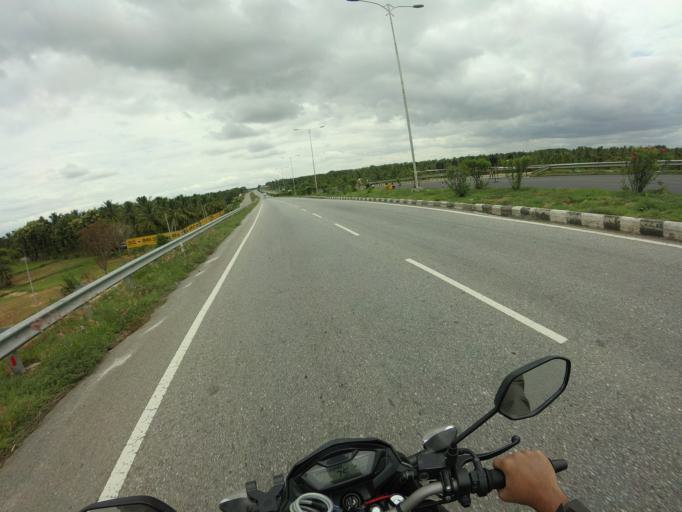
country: IN
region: Karnataka
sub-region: Tumkur
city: Kunigal
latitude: 13.0032
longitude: 76.9536
